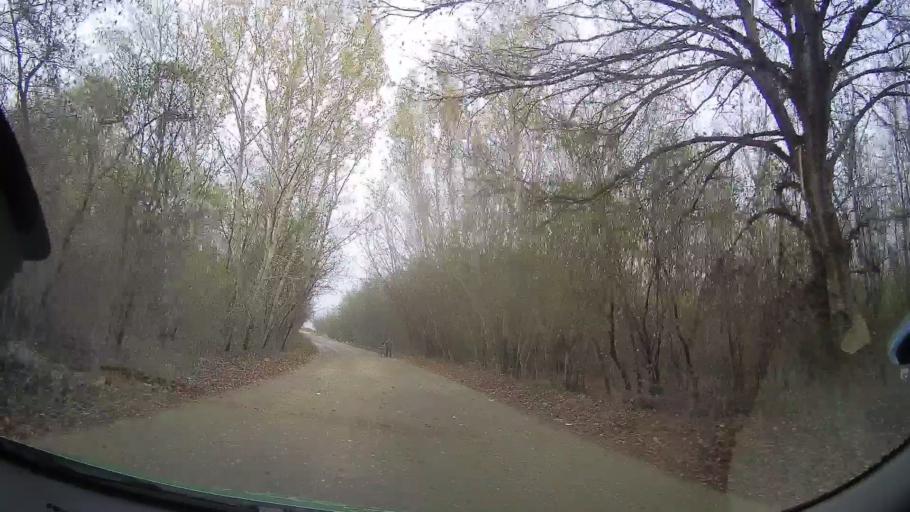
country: RO
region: Ialomita
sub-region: Comuna Fierbinti-Targ
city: Fierbinti-Targ
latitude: 44.6820
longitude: 26.3486
